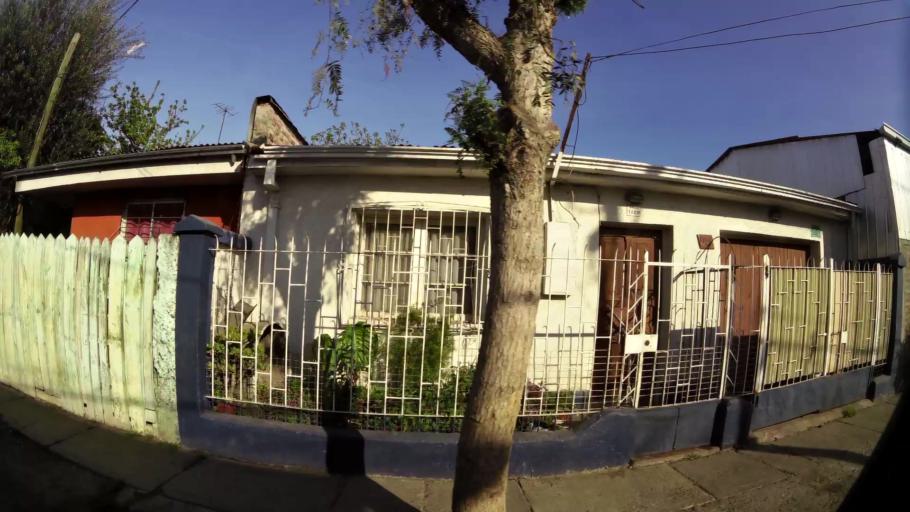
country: CL
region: Santiago Metropolitan
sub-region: Provincia de Santiago
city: Lo Prado
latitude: -33.4385
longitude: -70.7492
